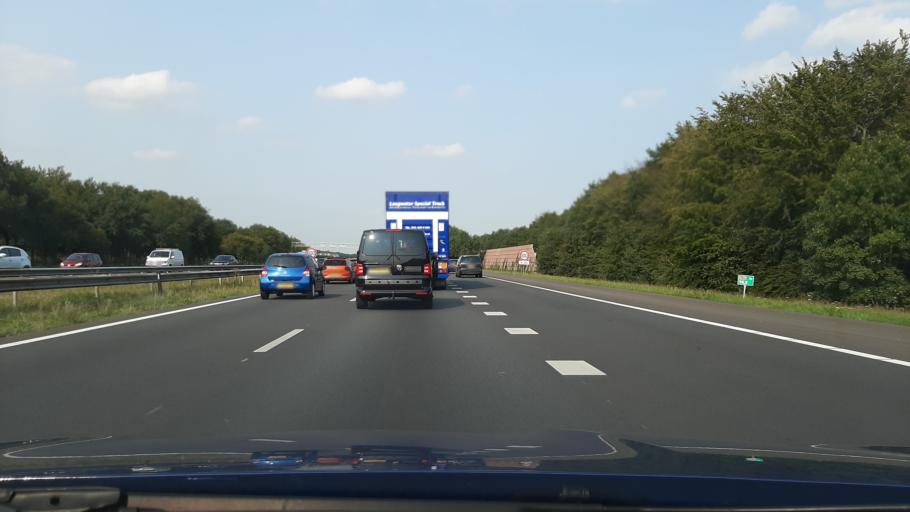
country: NL
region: North Holland
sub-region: Gemeente Laren
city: Laren
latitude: 52.2396
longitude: 5.2455
